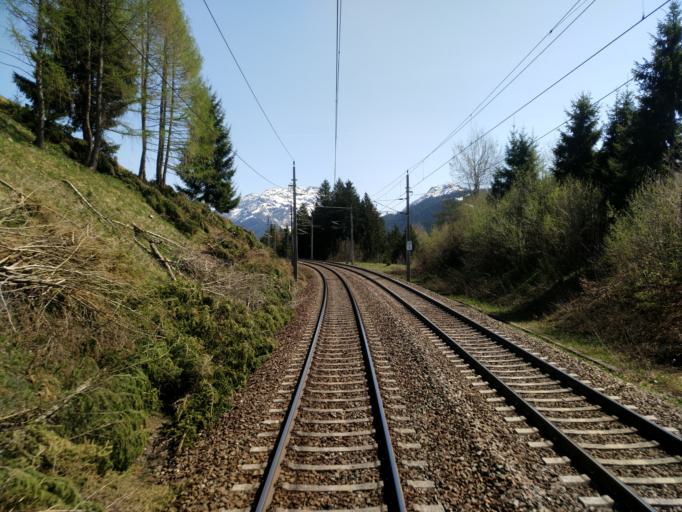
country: AT
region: Tyrol
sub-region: Politischer Bezirk Kitzbuhel
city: Fieberbrunn
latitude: 47.4796
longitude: 12.5432
